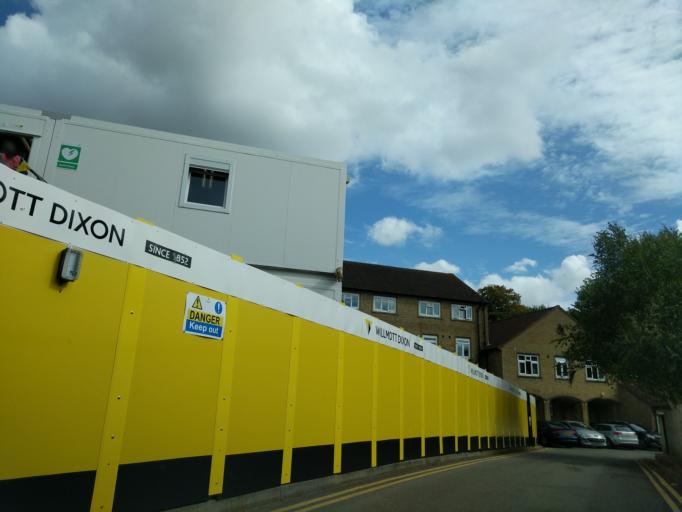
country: GB
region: England
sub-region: Oxfordshire
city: Cowley
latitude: 51.7610
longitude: -1.2179
